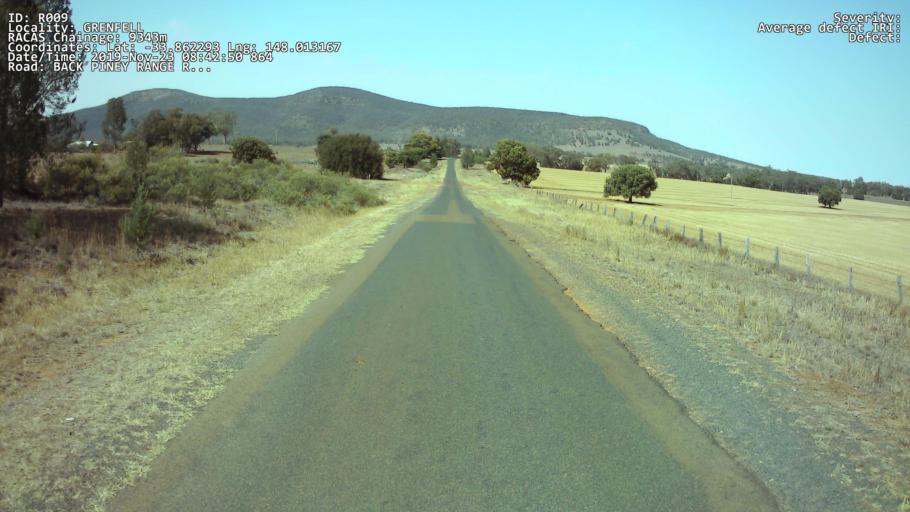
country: AU
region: New South Wales
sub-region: Weddin
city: Grenfell
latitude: -33.8622
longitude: 148.0133
